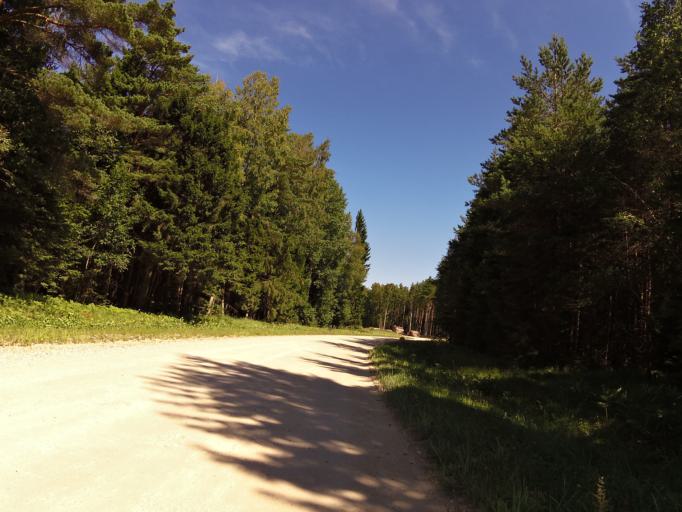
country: EE
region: Hiiumaa
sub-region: Kaerdla linn
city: Kardla
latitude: 58.9231
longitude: 22.3663
